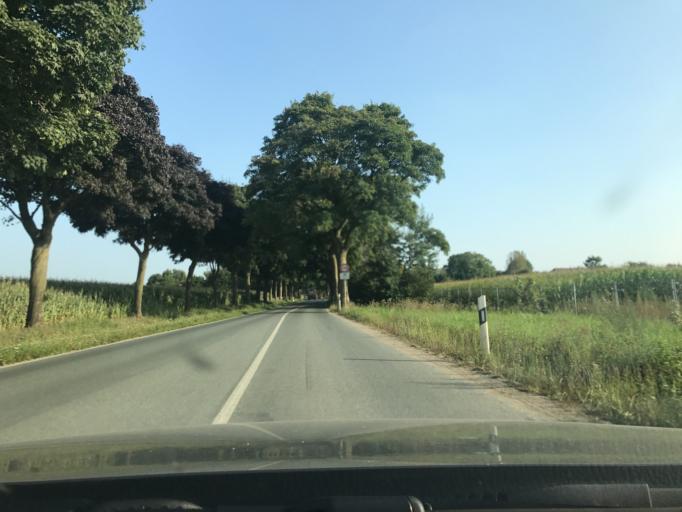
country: DE
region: North Rhine-Westphalia
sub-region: Regierungsbezirk Dusseldorf
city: Kleve
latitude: 51.7453
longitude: 6.1949
